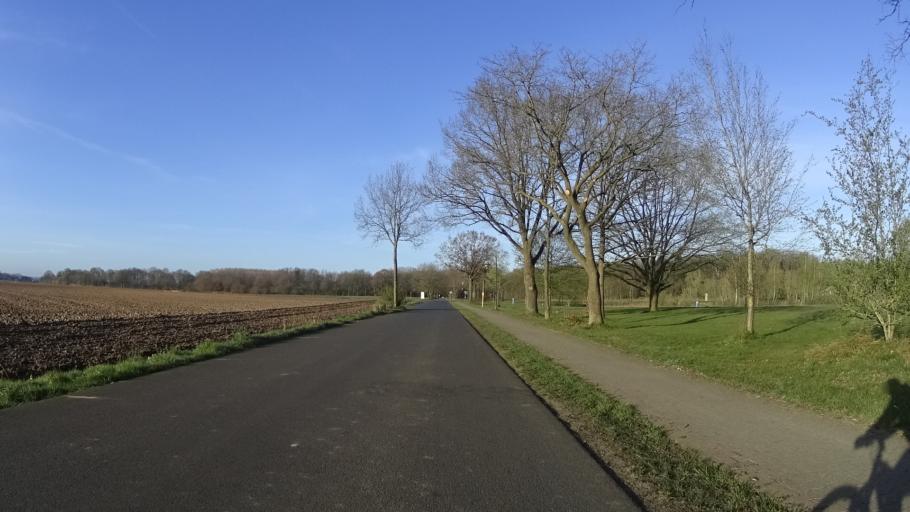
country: DE
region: Lower Saxony
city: Lathen
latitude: 52.8586
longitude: 7.3082
